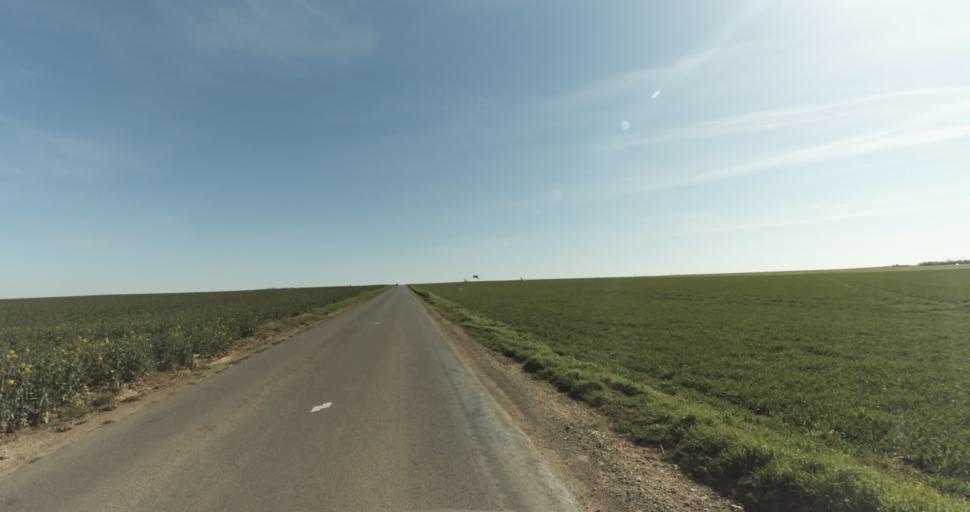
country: FR
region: Lower Normandy
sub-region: Departement du Calvados
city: Saint-Pierre-sur-Dives
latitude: 49.0016
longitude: -0.0482
